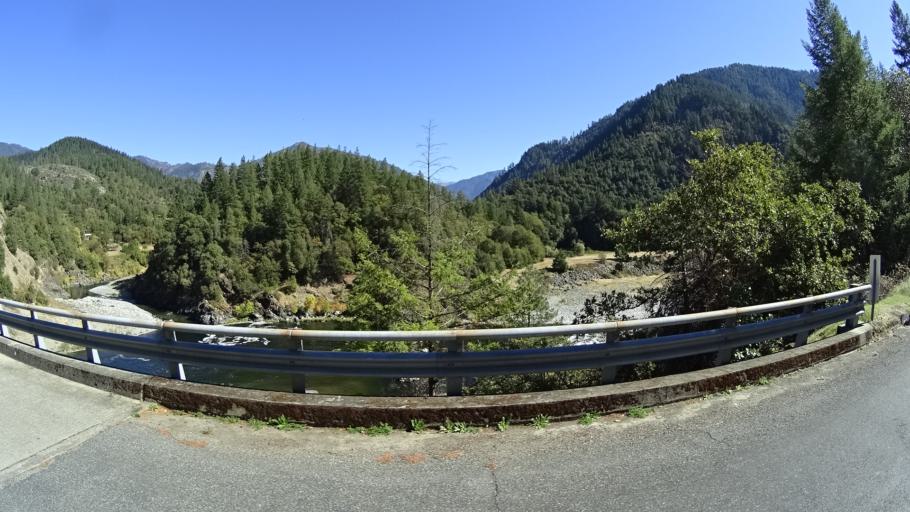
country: US
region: California
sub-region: Siskiyou County
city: Happy Camp
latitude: 41.3764
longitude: -123.4950
